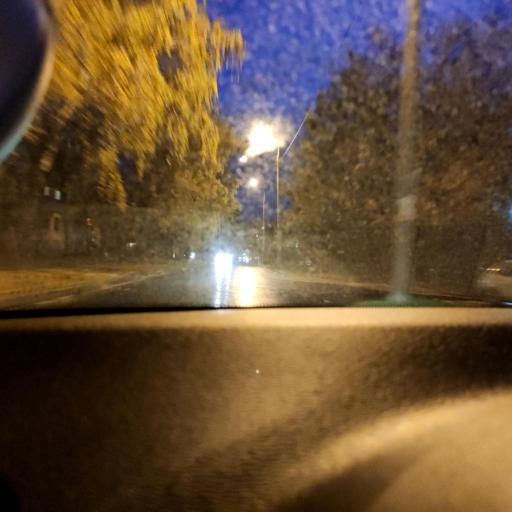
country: RU
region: Samara
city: Samara
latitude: 53.2179
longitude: 50.2274
